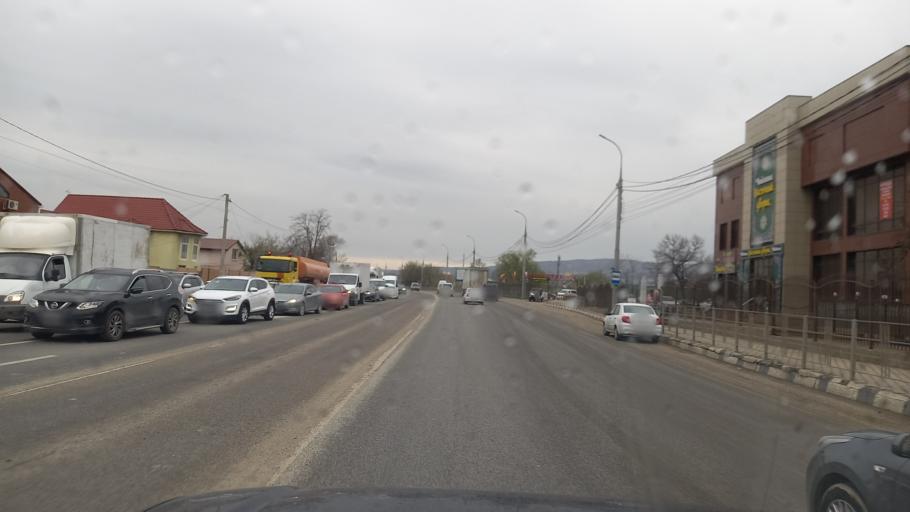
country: RU
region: Krasnodarskiy
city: Gayduk
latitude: 44.7626
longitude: 37.7190
